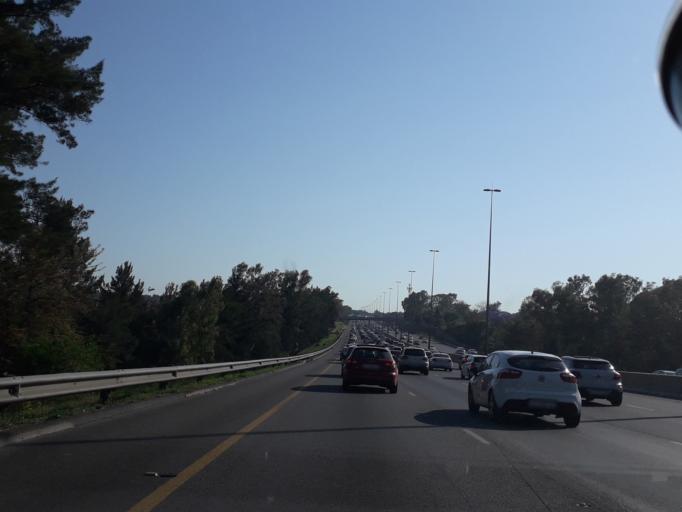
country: ZA
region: Gauteng
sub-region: City of Johannesburg Metropolitan Municipality
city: Diepsloot
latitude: -26.0523
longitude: 27.9941
